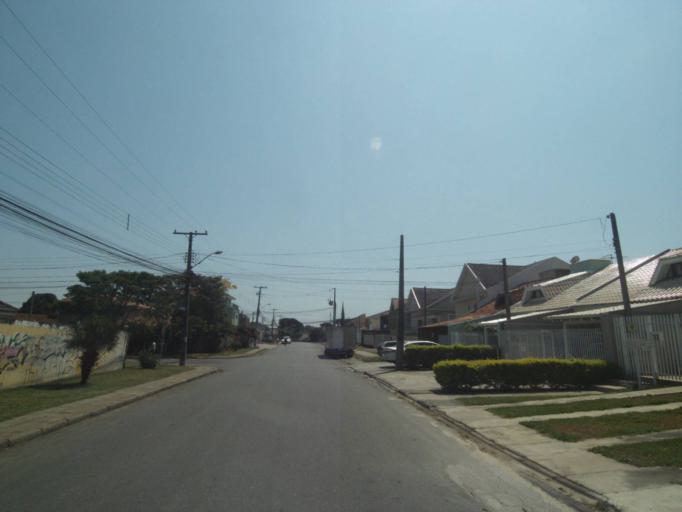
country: BR
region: Parana
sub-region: Sao Jose Dos Pinhais
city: Sao Jose dos Pinhais
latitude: -25.5166
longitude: -49.2641
